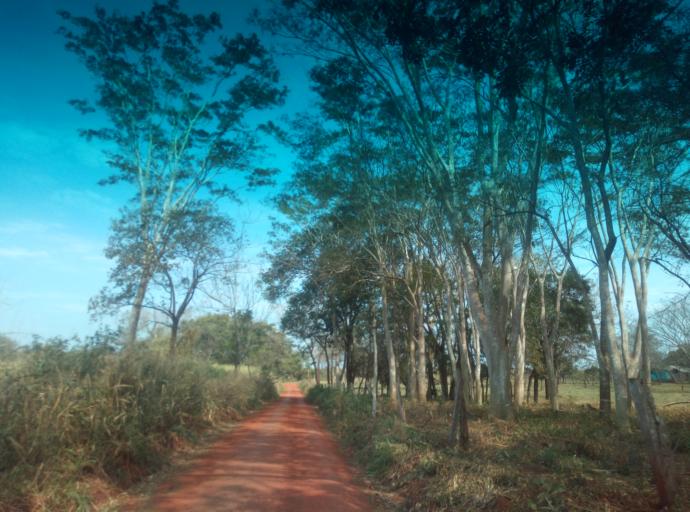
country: PY
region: Caaguazu
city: Carayao
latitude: -25.2030
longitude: -56.2528
